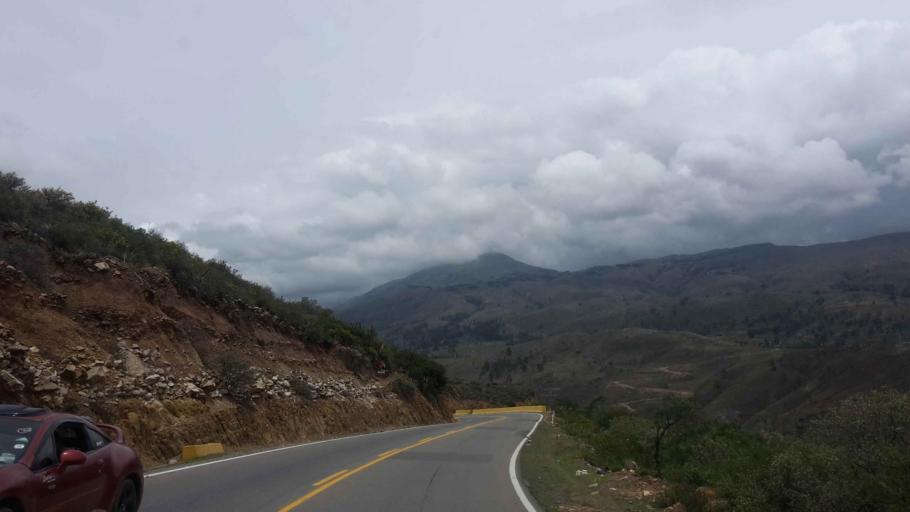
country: BO
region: Cochabamba
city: Punata
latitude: -17.4937
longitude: -65.7816
